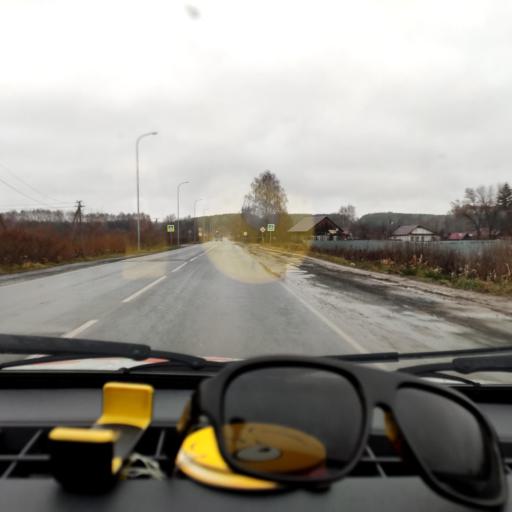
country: RU
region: Bashkortostan
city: Iglino
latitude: 54.8301
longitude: 56.3912
